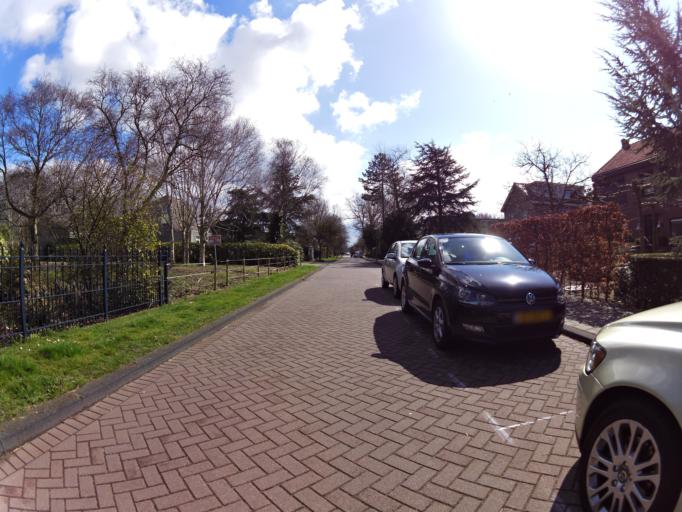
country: NL
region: South Holland
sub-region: Gemeente Hellevoetsluis
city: Nieuw-Helvoet
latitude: 51.8735
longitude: 4.0654
